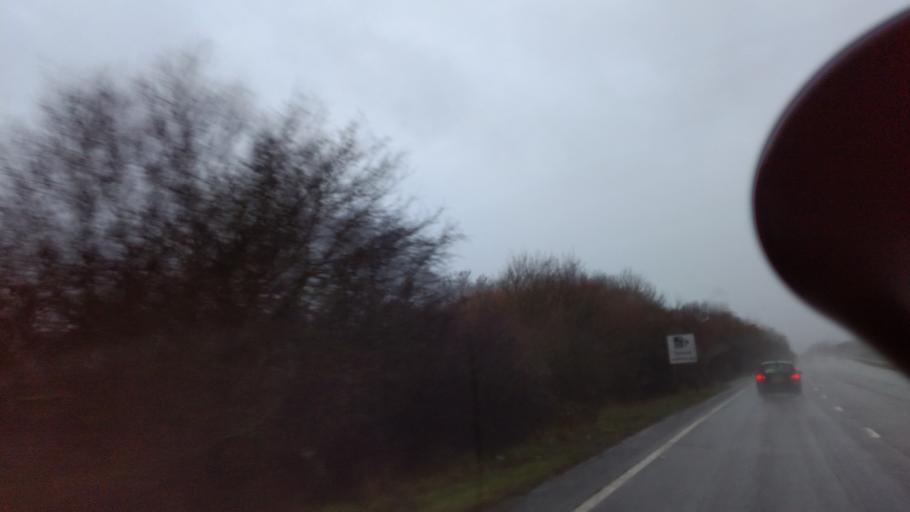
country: GB
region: England
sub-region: West Sussex
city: Goring-by-Sea
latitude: 50.8387
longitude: -0.4606
